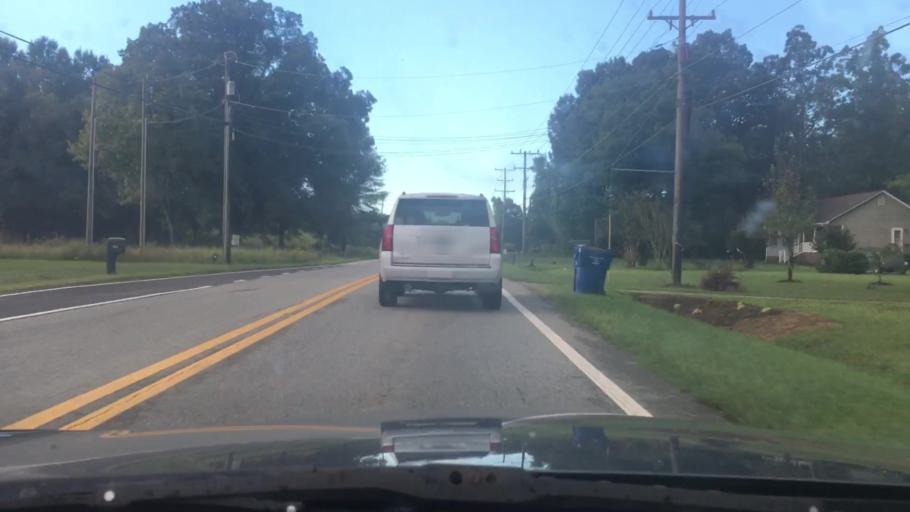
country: US
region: North Carolina
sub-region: Alamance County
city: Green Level
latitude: 36.1358
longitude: -79.3449
